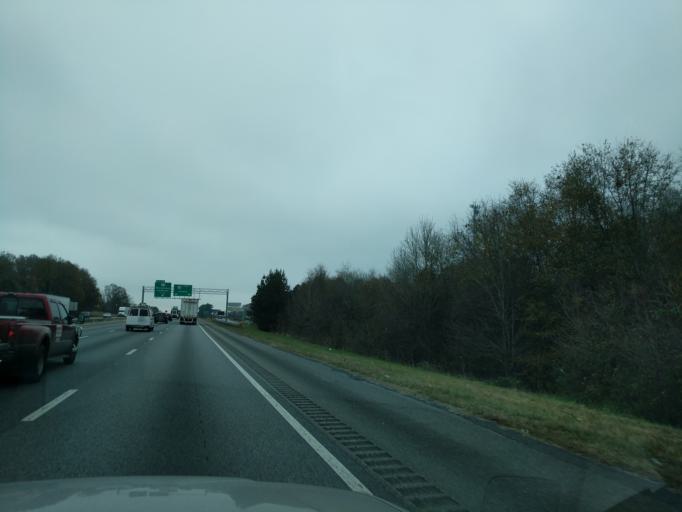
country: US
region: South Carolina
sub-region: Anderson County
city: Piedmont
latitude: 34.7097
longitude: -82.4997
